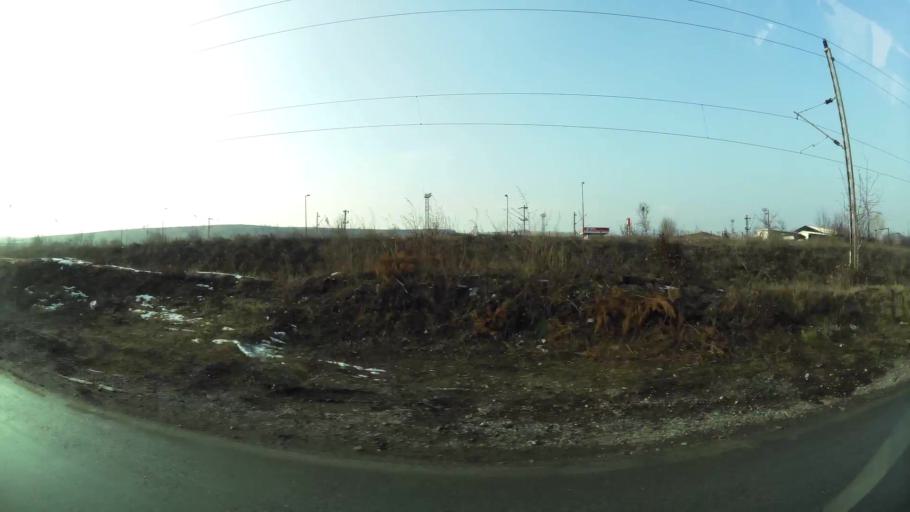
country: MK
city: Miladinovci
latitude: 41.9903
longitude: 21.6531
